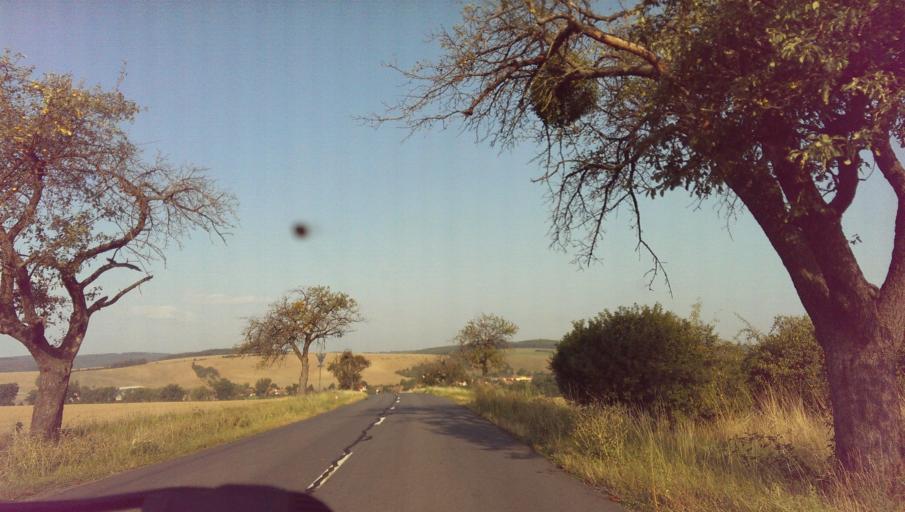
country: CZ
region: Zlin
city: Korycany
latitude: 49.1086
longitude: 17.1510
